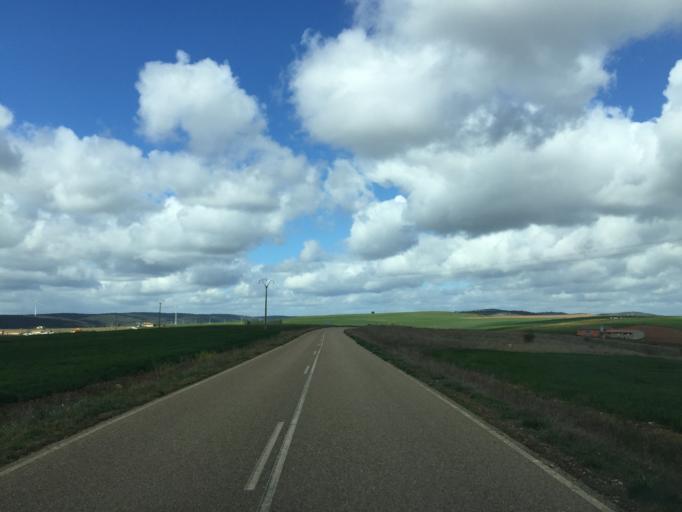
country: ES
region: Castille and Leon
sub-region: Provincia de Zamora
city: Manzanal del Barco
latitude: 41.5849
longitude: -5.9552
